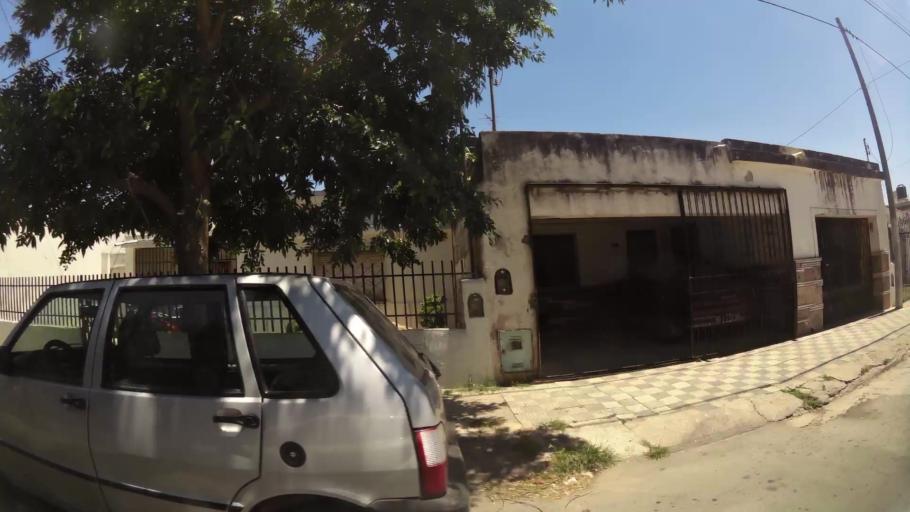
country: AR
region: Cordoba
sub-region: Departamento de Capital
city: Cordoba
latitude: -31.3799
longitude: -64.1357
